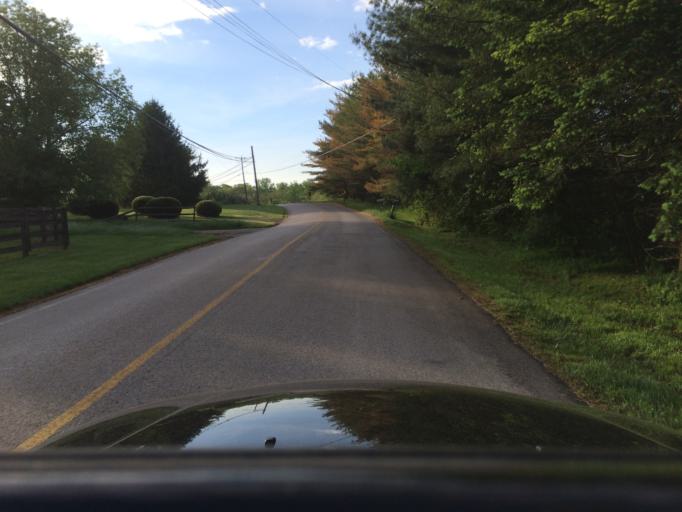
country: US
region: Maryland
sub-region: Howard County
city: Highland
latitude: 39.2187
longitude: -76.9985
